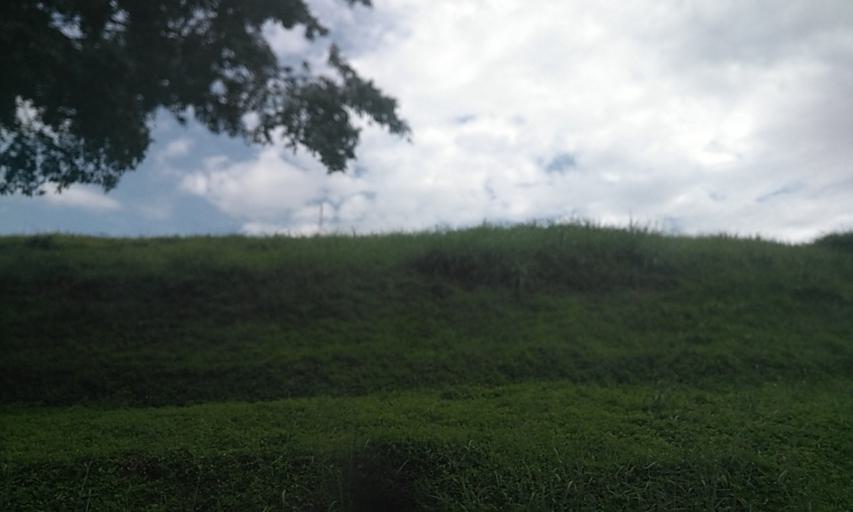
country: UG
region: Central Region
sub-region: Kampala District
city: Kampala
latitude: 0.3260
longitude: 32.5913
